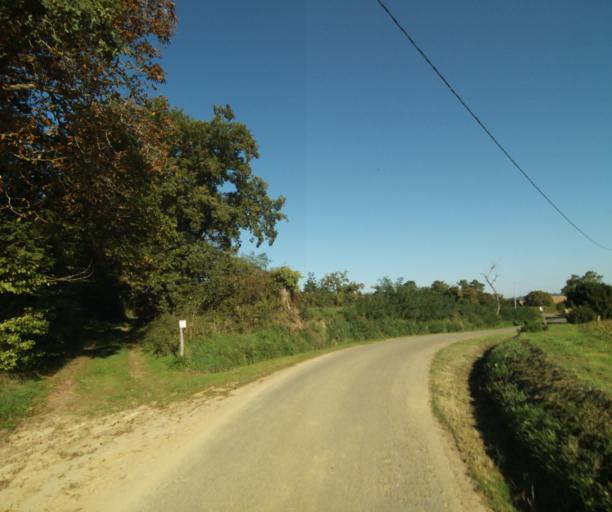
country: FR
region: Midi-Pyrenees
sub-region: Departement du Gers
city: Cazaubon
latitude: 43.9145
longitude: 0.0005
